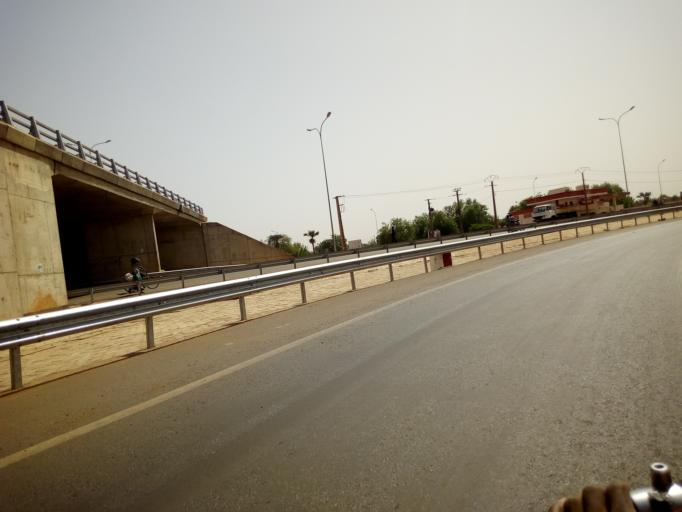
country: ML
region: Segou
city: Segou
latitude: 13.4373
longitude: -6.2386
